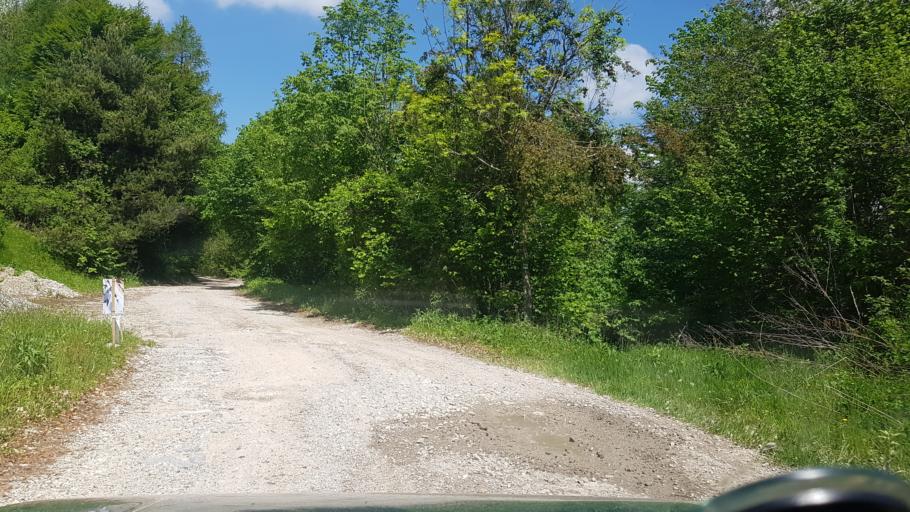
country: IT
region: Friuli Venezia Giulia
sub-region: Provincia di Udine
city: Pulfero
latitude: 46.1819
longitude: 13.4303
